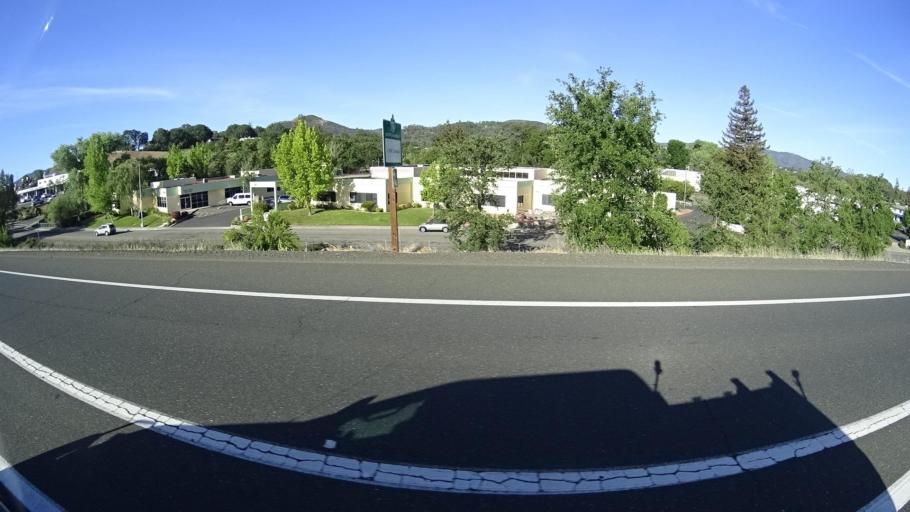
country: US
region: California
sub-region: Lake County
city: Lakeport
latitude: 39.0357
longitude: -122.9260
